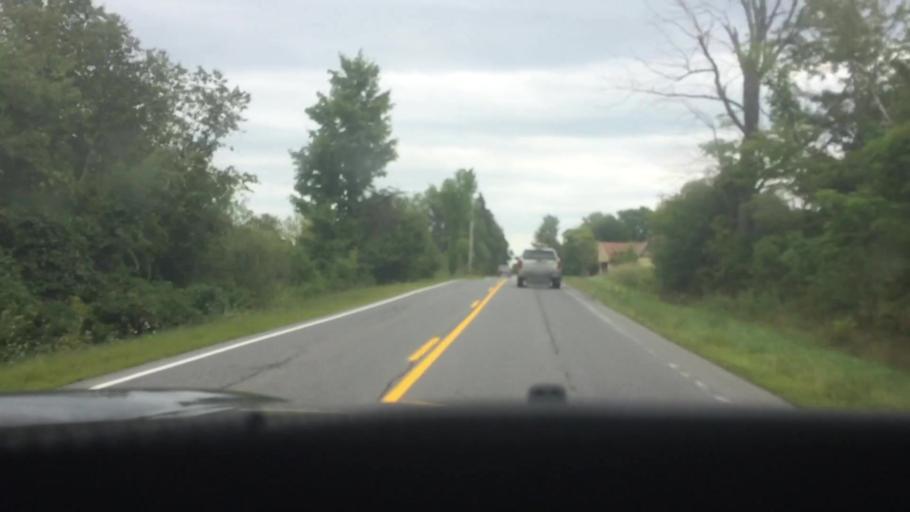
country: US
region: New York
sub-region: St. Lawrence County
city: Canton
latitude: 44.5373
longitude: -75.1684
